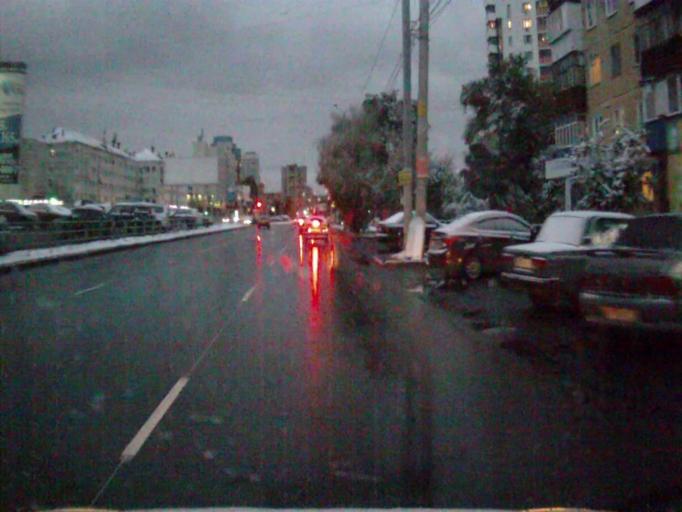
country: RU
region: Chelyabinsk
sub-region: Gorod Chelyabinsk
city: Chelyabinsk
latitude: 55.1493
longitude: 61.3917
